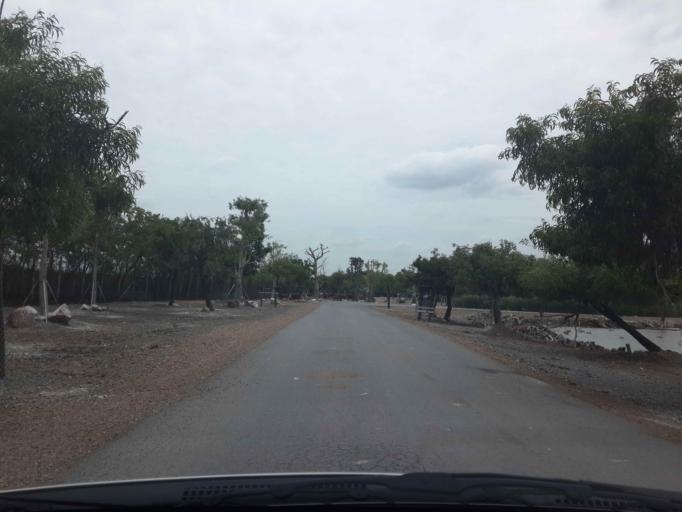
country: TH
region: Bangkok
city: Khan Na Yao
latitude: 13.8643
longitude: 100.6995
